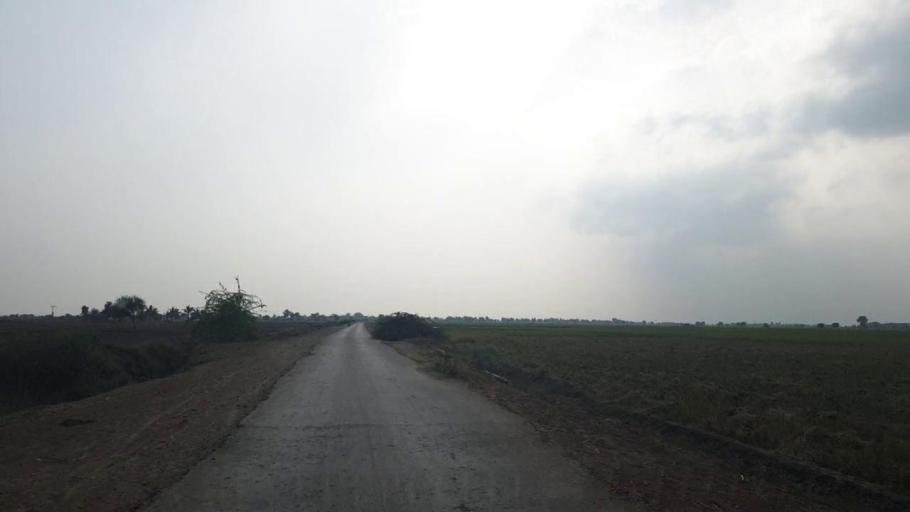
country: PK
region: Sindh
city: Badin
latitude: 24.6495
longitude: 68.6993
